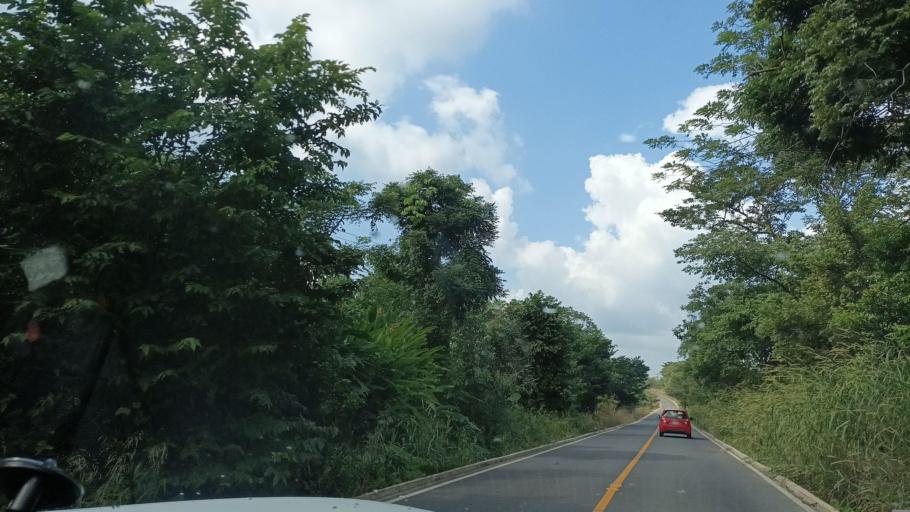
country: MX
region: Tabasco
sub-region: Huimanguillo
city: Francisco Rueda
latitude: 17.7397
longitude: -94.1072
